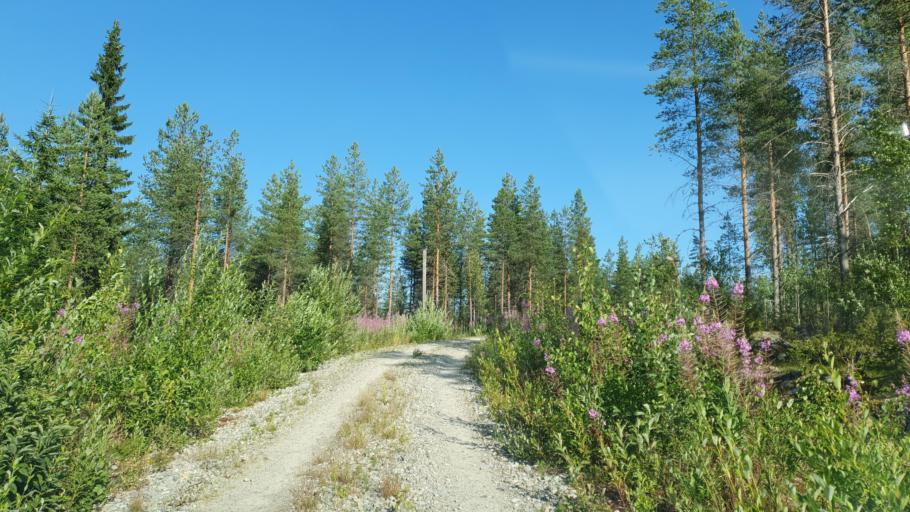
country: FI
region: Kainuu
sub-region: Kehys-Kainuu
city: Kuhmo
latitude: 64.0026
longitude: 29.7733
